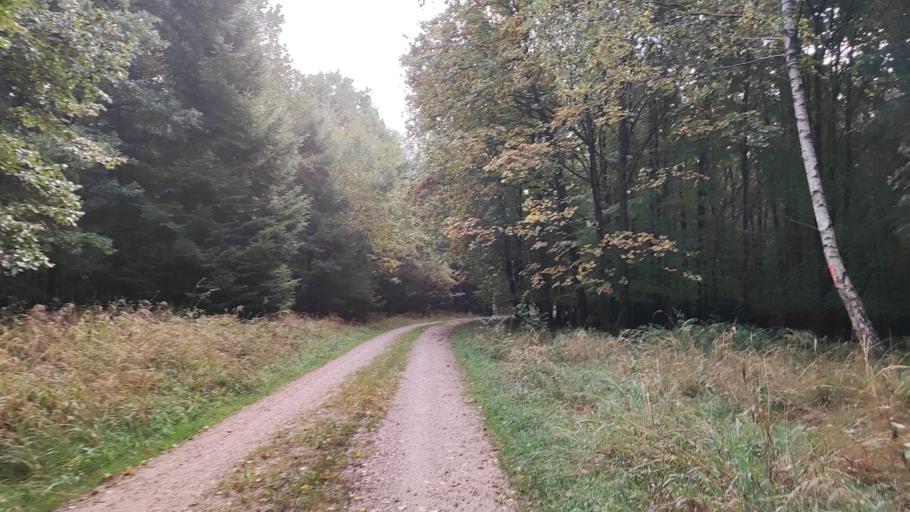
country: DE
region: Bavaria
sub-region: Swabia
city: Welden
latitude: 48.4274
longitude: 10.6329
